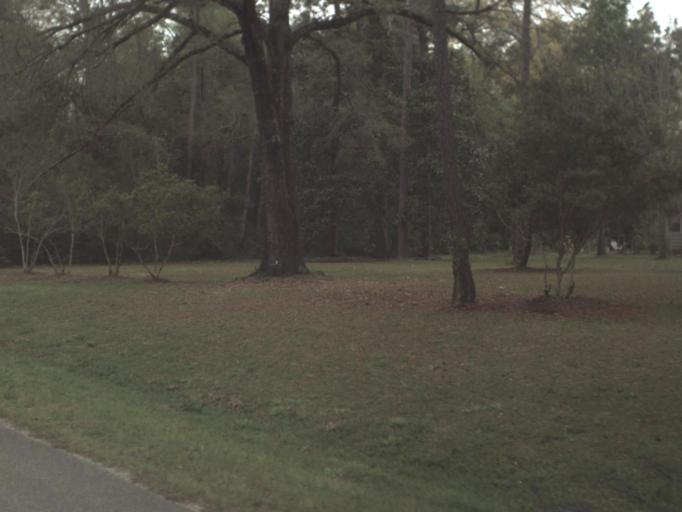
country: US
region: Florida
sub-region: Gadsden County
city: Gretna
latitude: 30.5502
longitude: -84.6769
